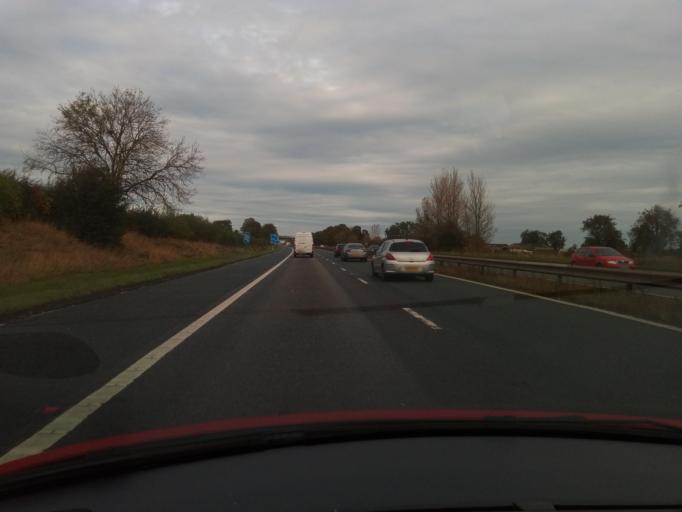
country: GB
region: England
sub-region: Darlington
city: High Coniscliffe
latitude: 54.4894
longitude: -1.6353
